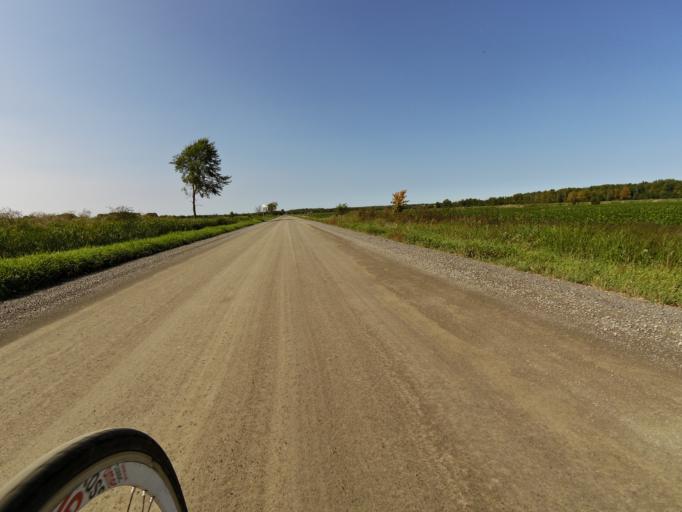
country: CA
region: Ontario
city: Arnprior
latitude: 45.3747
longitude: -76.1435
